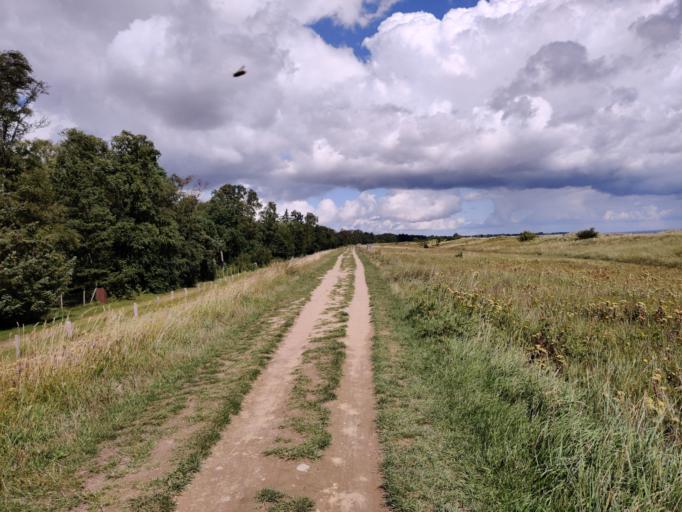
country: DK
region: Zealand
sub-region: Guldborgsund Kommune
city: Nykobing Falster
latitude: 54.6926
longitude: 11.9708
